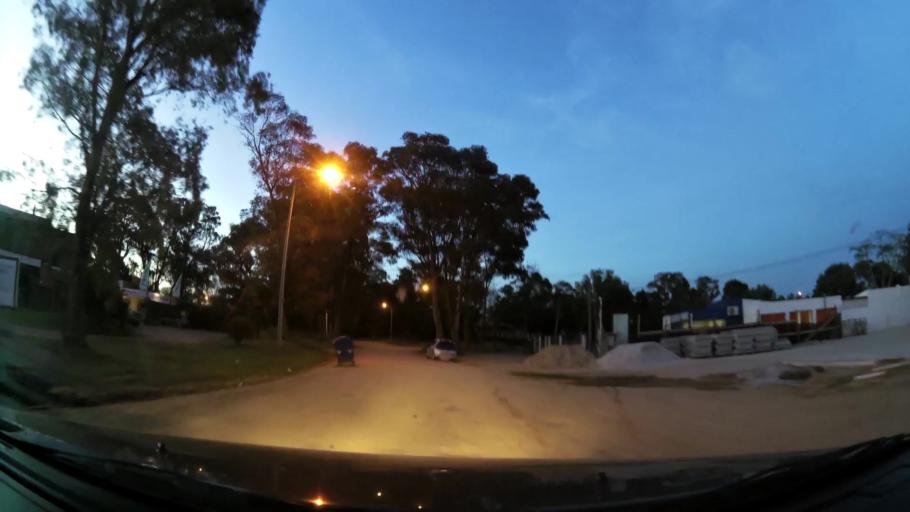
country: UY
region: Canelones
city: Atlantida
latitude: -34.7650
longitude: -55.7558
